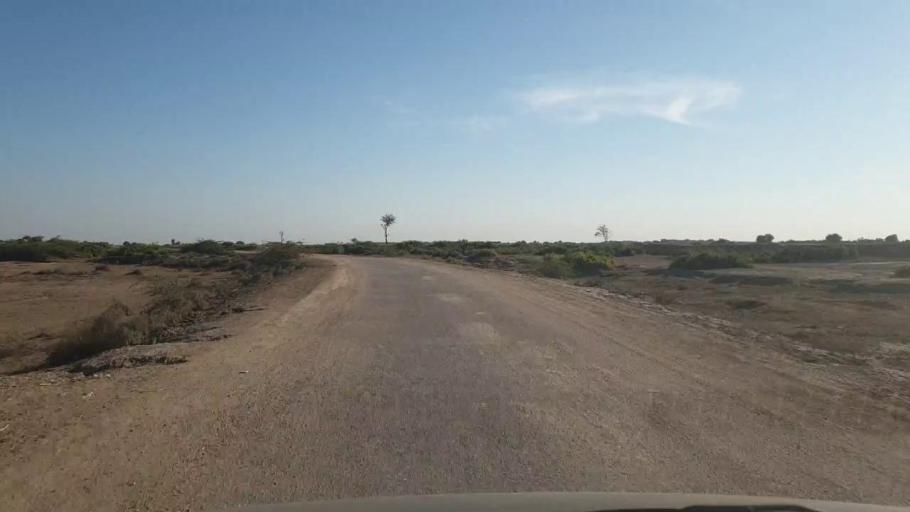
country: PK
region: Sindh
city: Dhoro Naro
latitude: 25.4287
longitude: 69.5329
